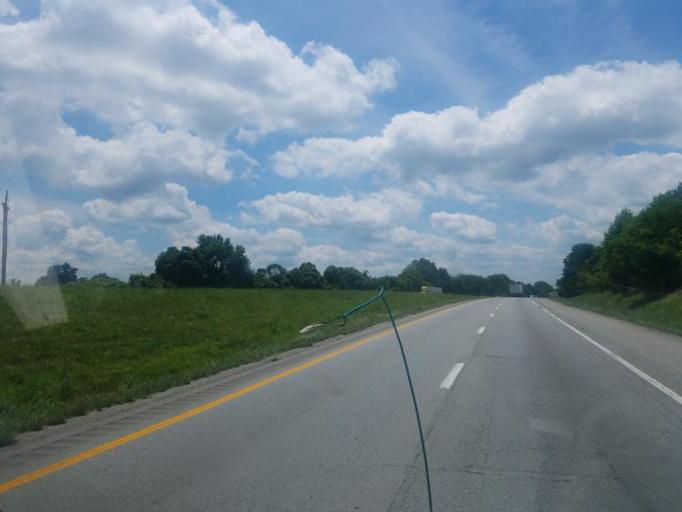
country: US
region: Kentucky
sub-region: Oldham County
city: La Grange
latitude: 38.4135
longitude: -85.3457
